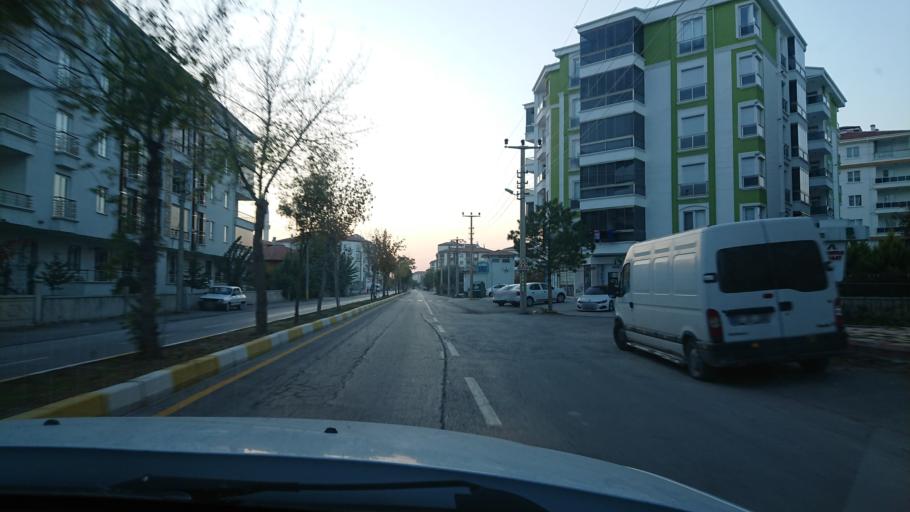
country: TR
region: Aksaray
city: Aksaray
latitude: 38.3605
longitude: 34.0180
